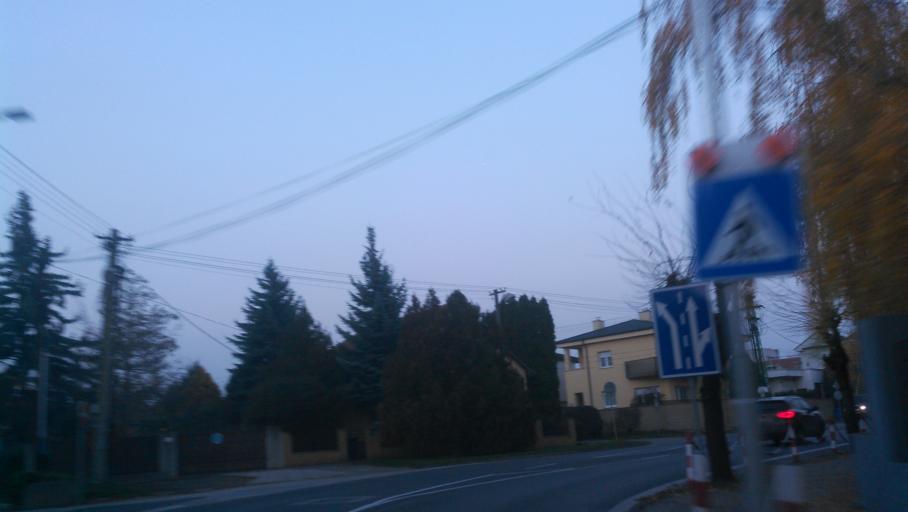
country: SK
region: Bratislavsky
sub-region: Okres Pezinok
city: Pezinok
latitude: 48.2869
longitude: 17.2736
